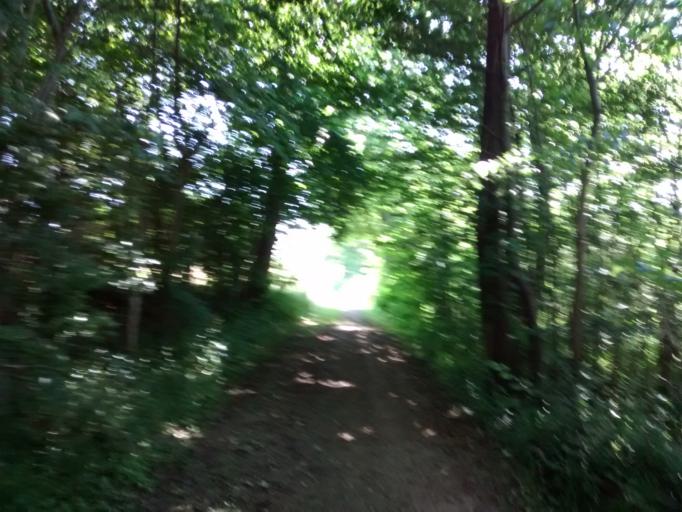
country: DK
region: Zealand
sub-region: Soro Kommune
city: Soro
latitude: 55.4538
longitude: 11.5825
